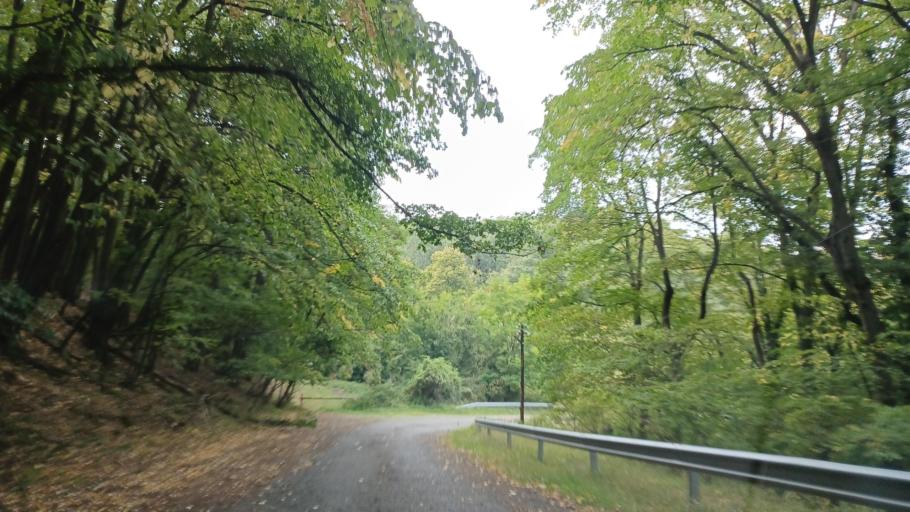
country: HU
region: Baranya
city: Mecseknadasd
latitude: 46.2015
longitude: 18.4530
